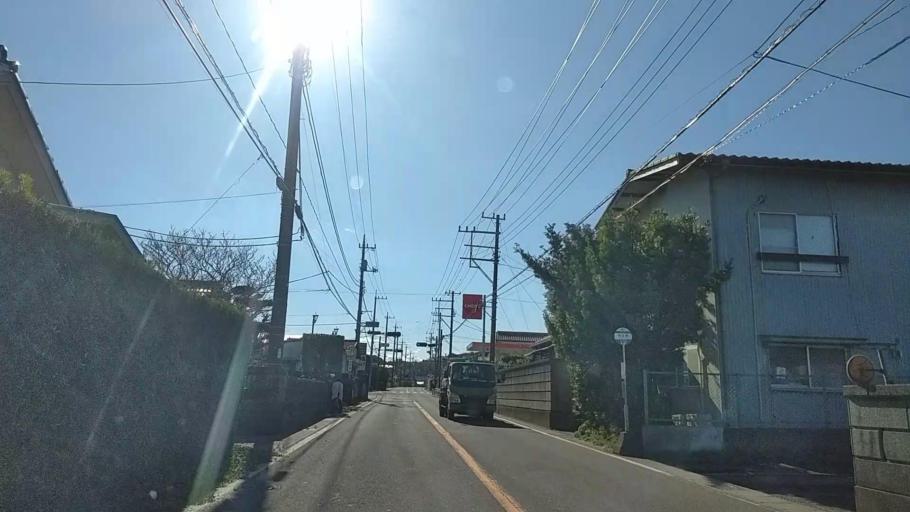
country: JP
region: Chiba
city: Tateyama
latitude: 34.9808
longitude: 139.8631
